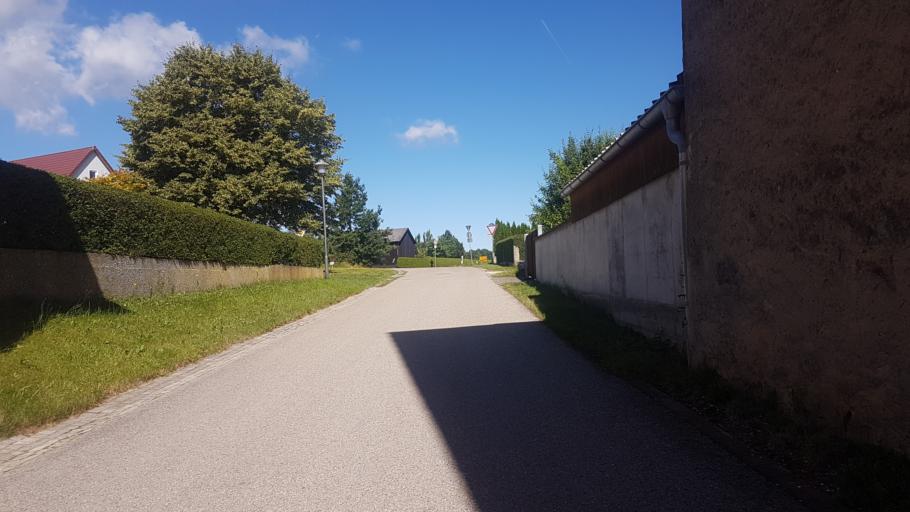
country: DE
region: Bavaria
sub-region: Regierungsbezirk Mittelfranken
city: Burgoberbach
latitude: 49.1932
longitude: 10.5691
